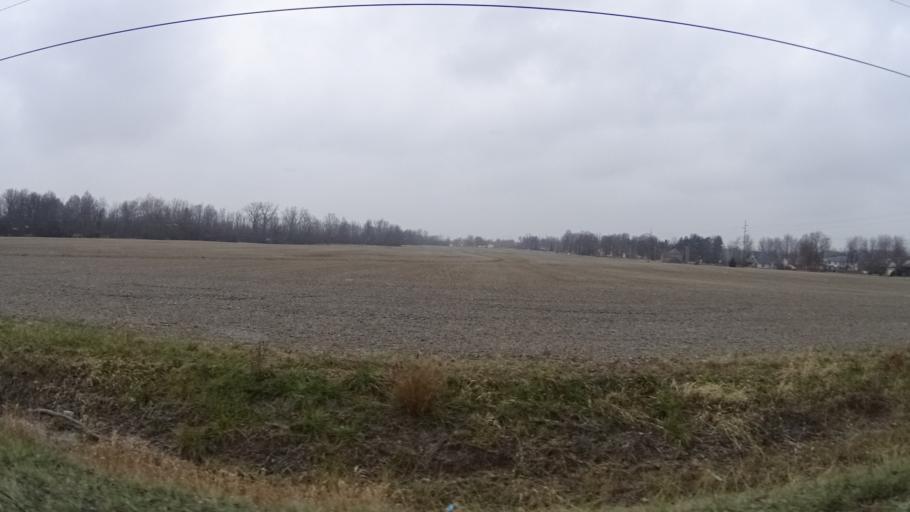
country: US
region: Ohio
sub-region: Lorain County
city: Oberlin
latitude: 41.2943
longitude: -82.2397
